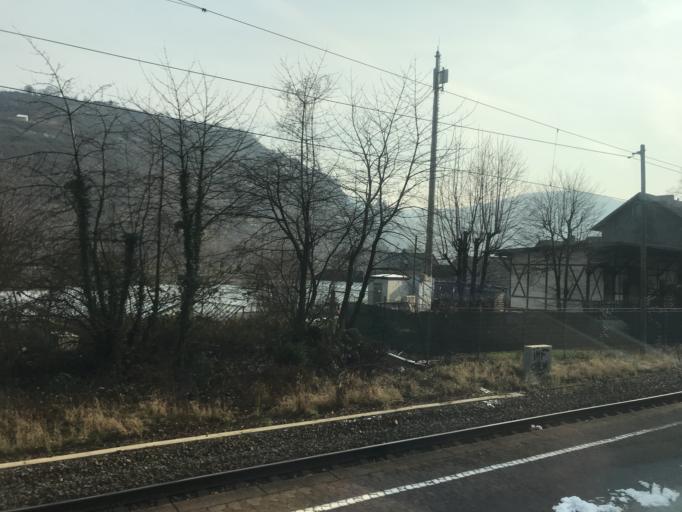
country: DE
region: Rheinland-Pfalz
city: Oberfell
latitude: 50.2560
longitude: 7.4383
